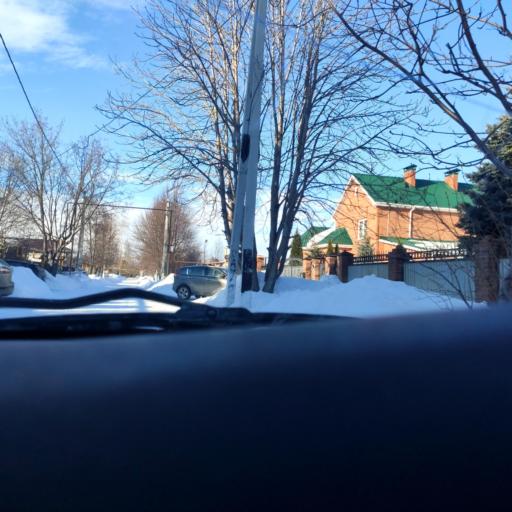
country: RU
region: Samara
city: Podstepki
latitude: 53.5140
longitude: 49.1563
